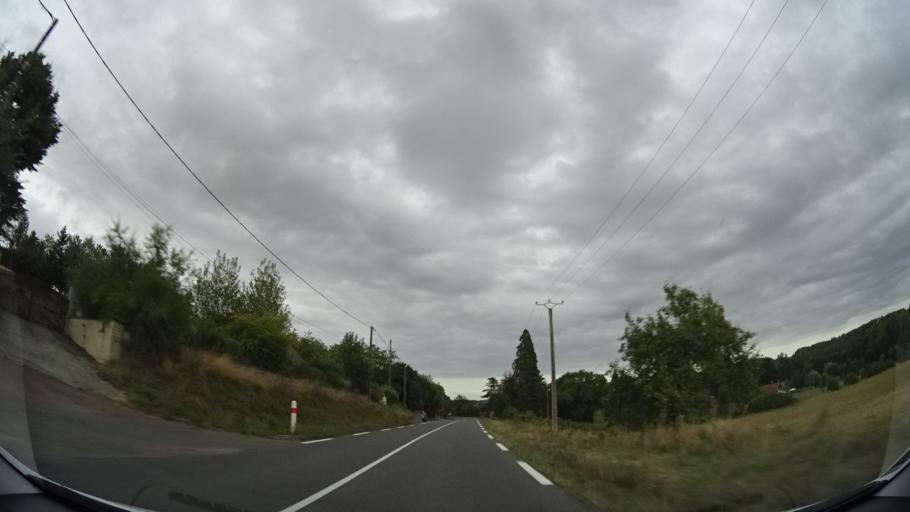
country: FR
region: Centre
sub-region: Departement du Loiret
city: Saint-Germain-des-Pres
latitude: 47.9341
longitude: 2.9017
